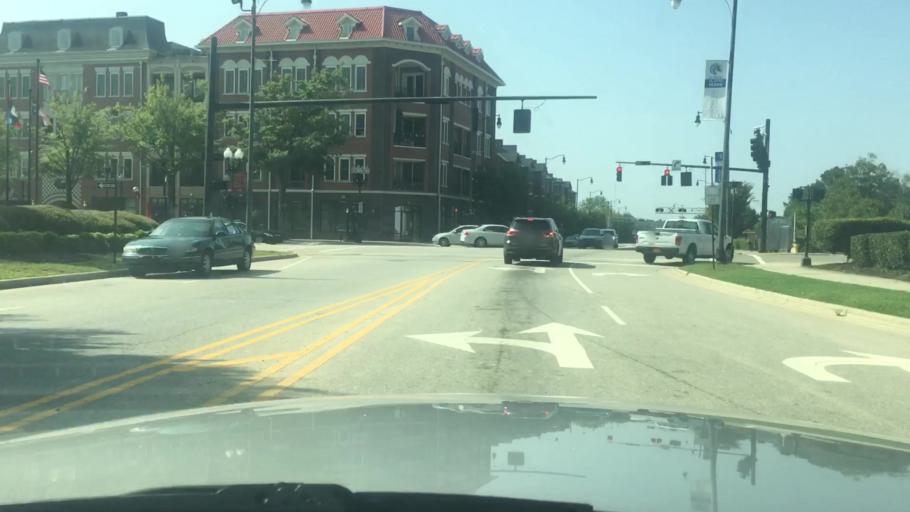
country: US
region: North Carolina
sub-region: Cumberland County
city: Fayetteville
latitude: 35.0544
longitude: -78.8820
